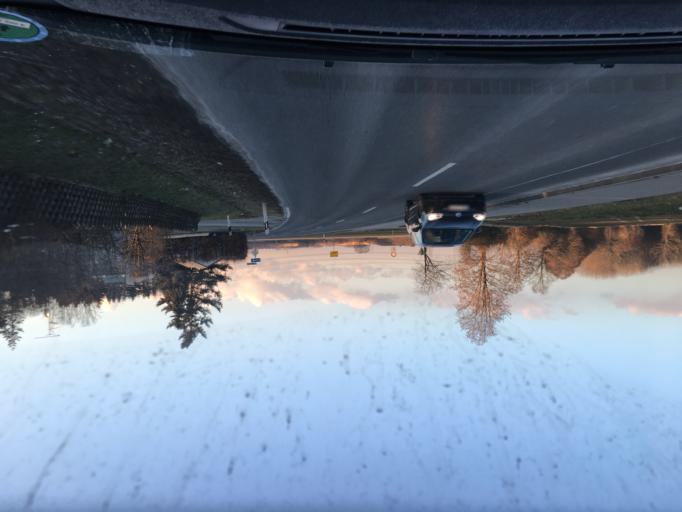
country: DE
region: North Rhine-Westphalia
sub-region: Regierungsbezirk Koln
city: Dueren
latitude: 50.8434
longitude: 6.4866
